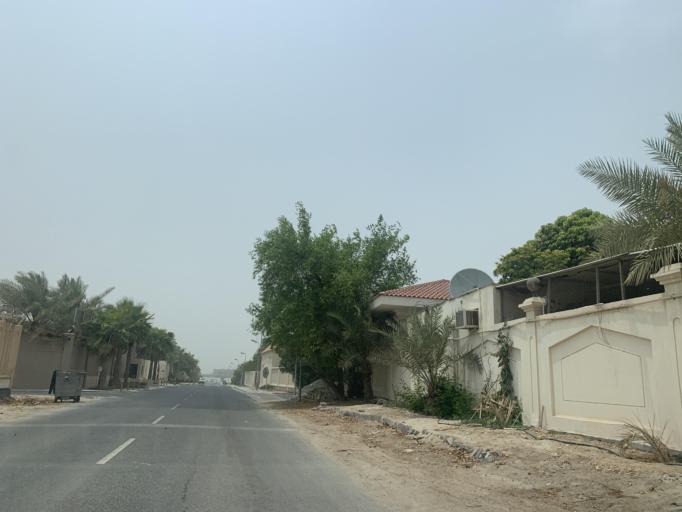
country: BH
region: Central Governorate
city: Madinat Hamad
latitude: 26.1667
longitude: 50.4796
